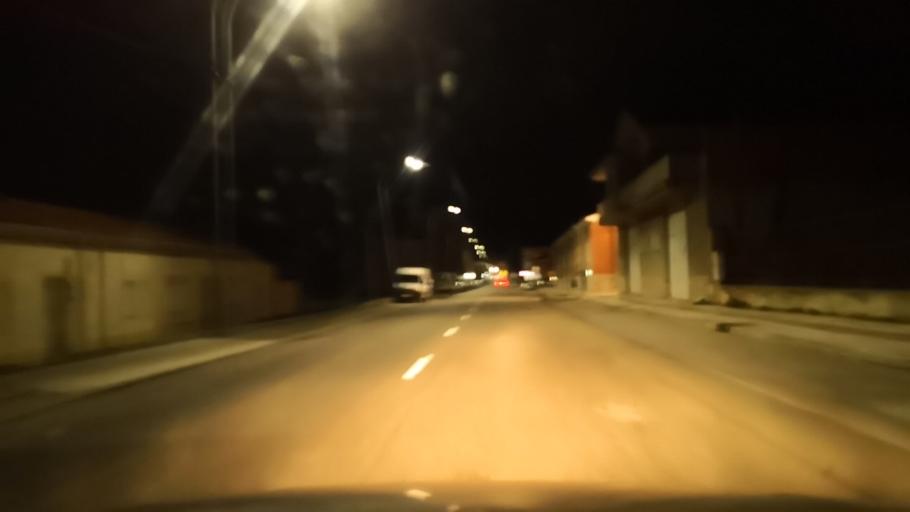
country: ES
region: Castille and Leon
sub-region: Provincia de Zamora
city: Benavente
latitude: 42.0081
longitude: -5.6704
